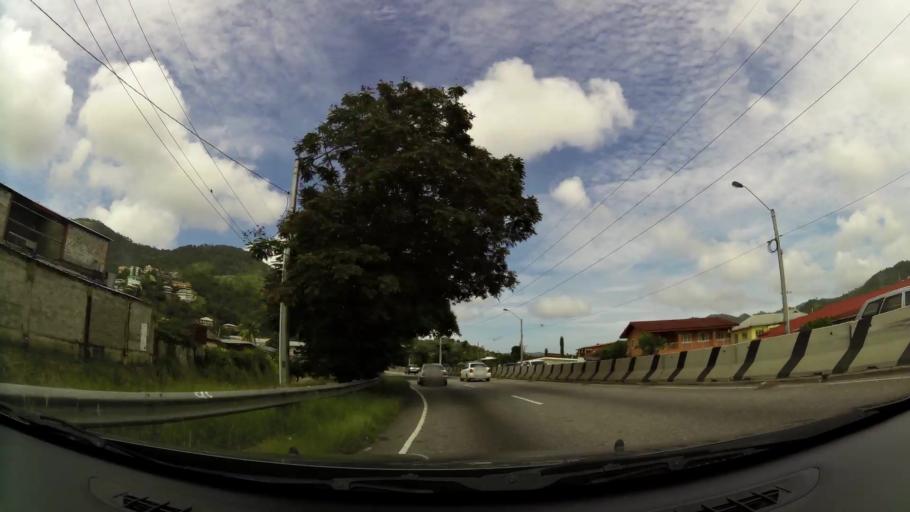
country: TT
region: Diego Martin
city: Petit Valley
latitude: 10.6921
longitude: -61.5535
